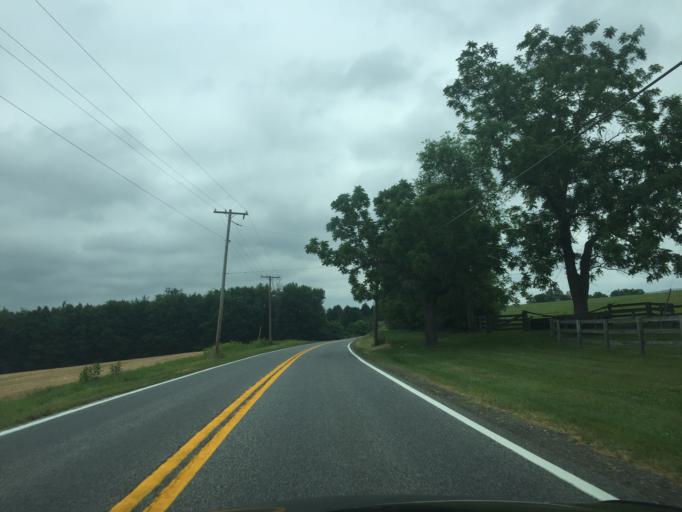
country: US
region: Maryland
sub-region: Harford County
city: Jarrettsville
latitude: 39.5676
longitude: -76.5225
